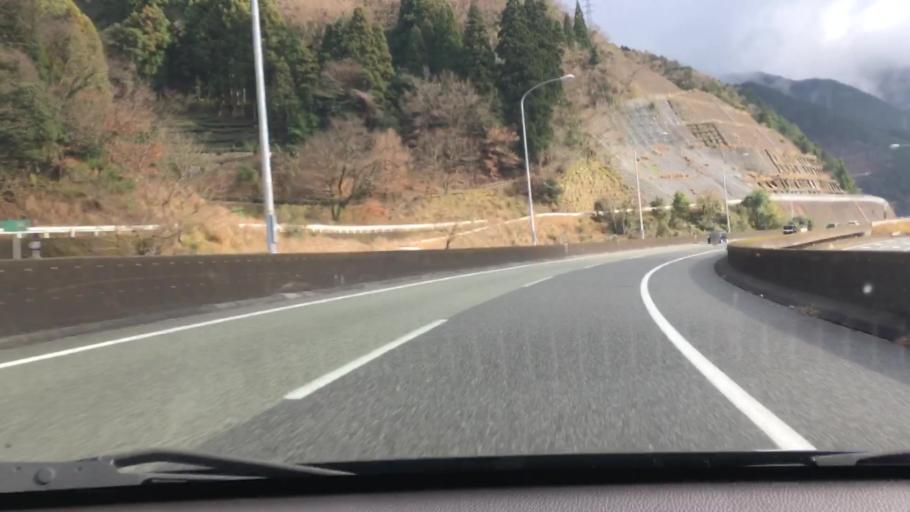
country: JP
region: Kumamoto
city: Yatsushiro
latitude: 32.4000
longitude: 130.7015
